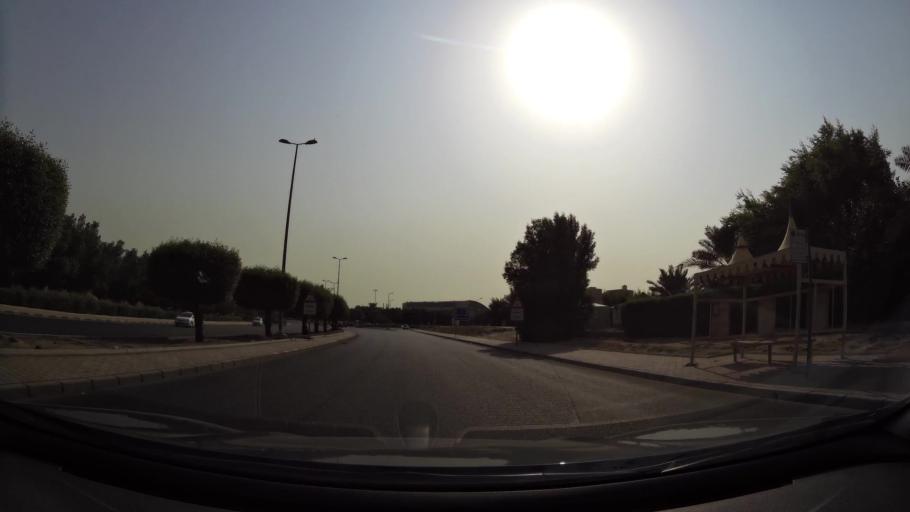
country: KW
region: Mubarak al Kabir
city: Sabah as Salim
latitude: 29.2580
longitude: 48.0628
